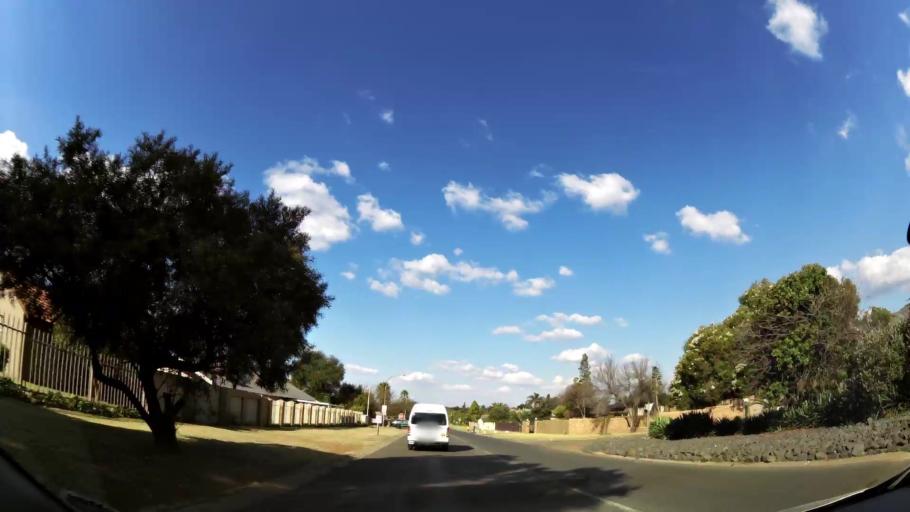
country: ZA
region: Mpumalanga
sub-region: Nkangala District Municipality
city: Witbank
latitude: -25.8940
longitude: 29.2323
